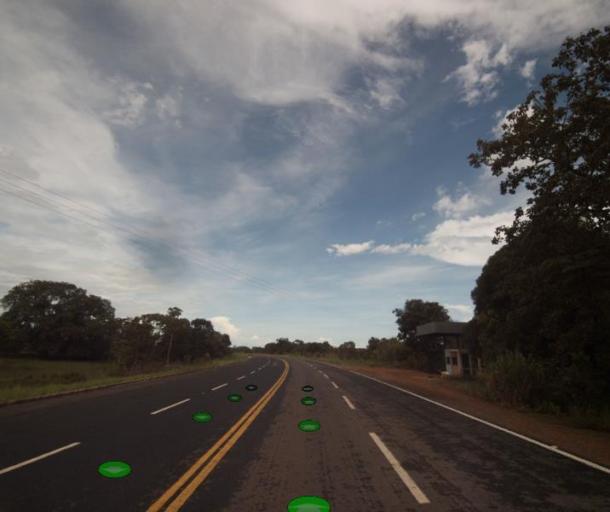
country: BR
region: Goias
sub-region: Sao Miguel Do Araguaia
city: Sao Miguel do Araguaia
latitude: -13.2316
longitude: -50.5656
